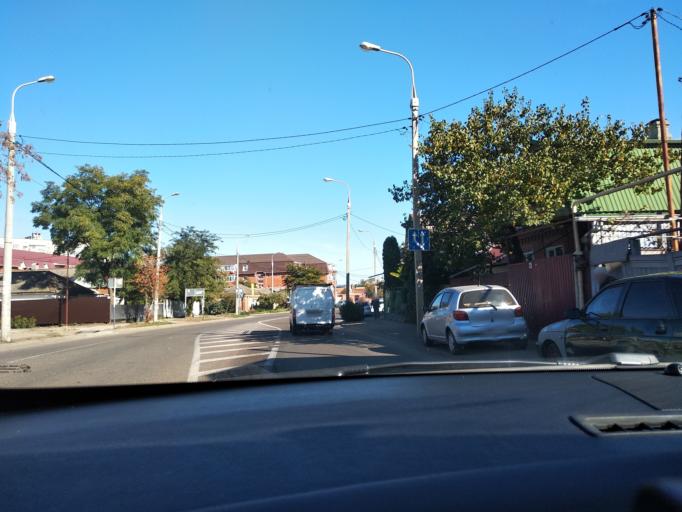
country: RU
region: Krasnodarskiy
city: Krasnodar
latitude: 45.0161
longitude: 38.9929
